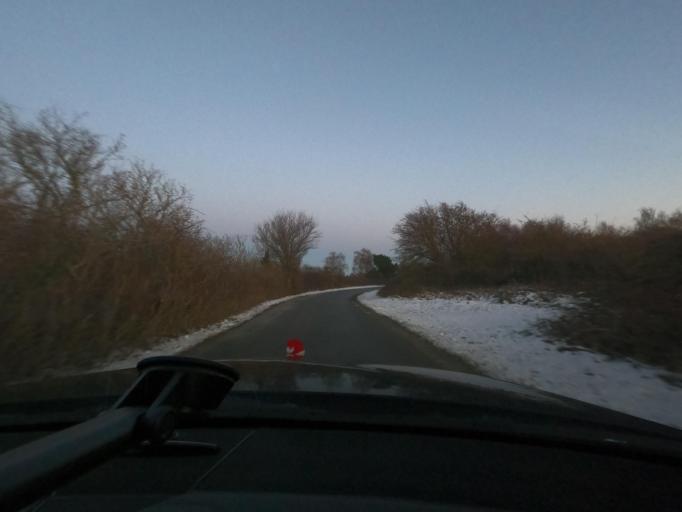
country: DK
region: South Denmark
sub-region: Sonderborg Kommune
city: Horuphav
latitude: 54.8658
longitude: 9.9056
